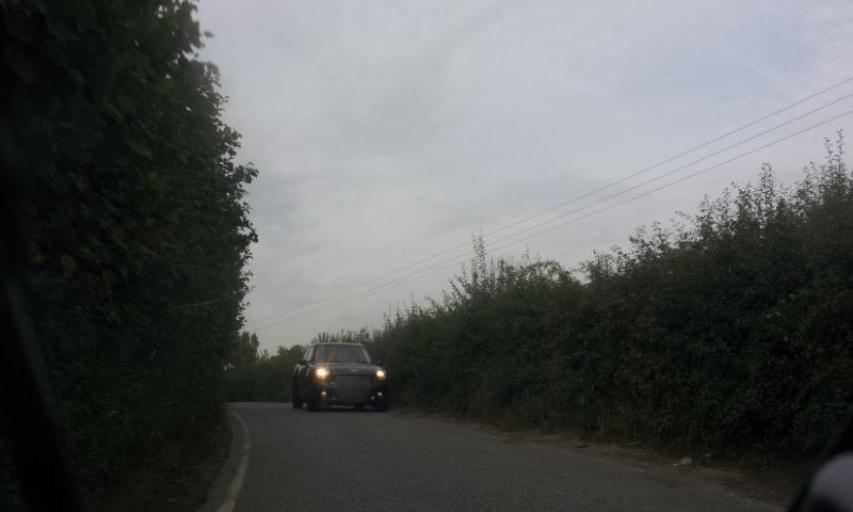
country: GB
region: England
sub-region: Kent
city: Tonbridge
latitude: 51.1725
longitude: 0.2749
